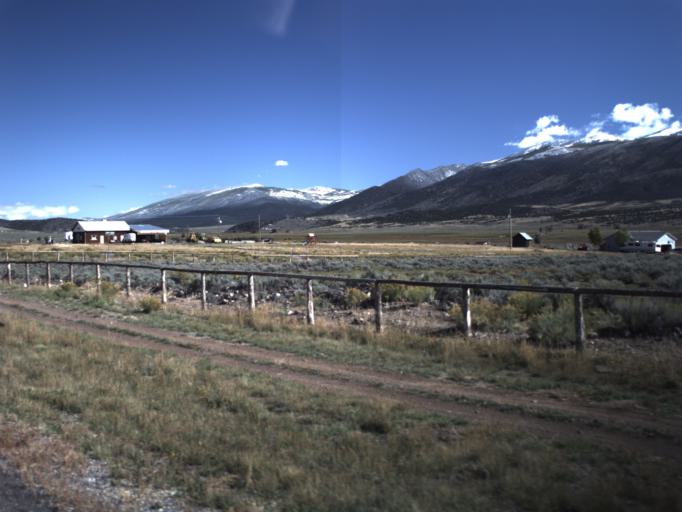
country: US
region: Utah
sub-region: Sevier County
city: Monroe
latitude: 38.5195
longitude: -111.8813
